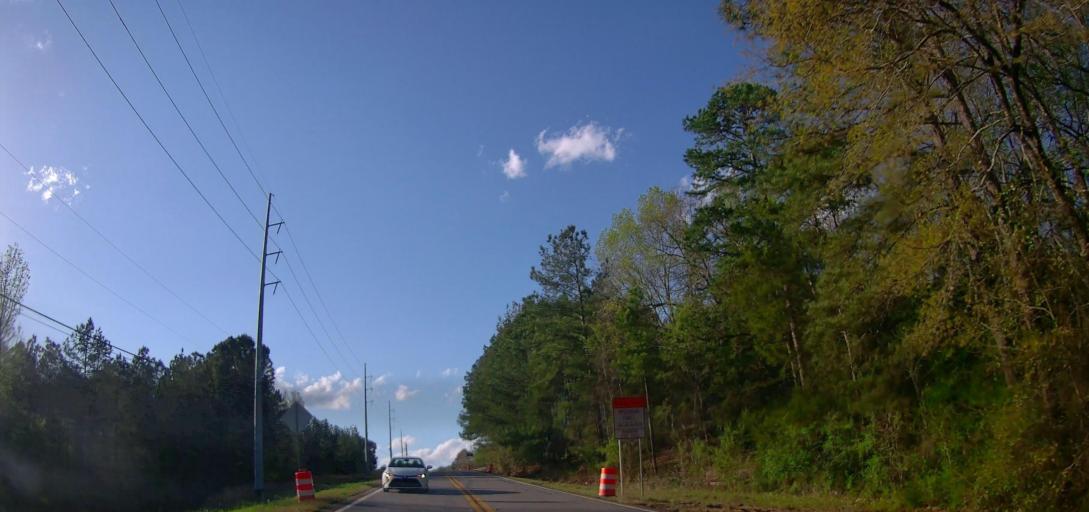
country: US
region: Georgia
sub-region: Baldwin County
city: Milledgeville
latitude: 33.1029
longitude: -83.2748
